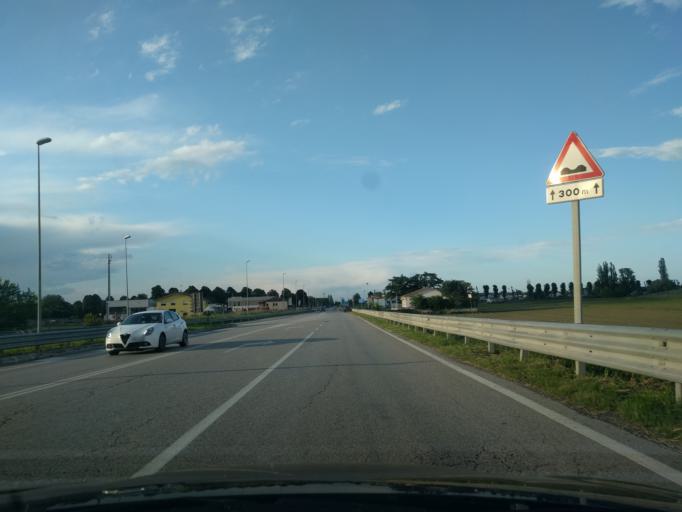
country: IT
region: Veneto
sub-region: Provincia di Rovigo
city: Polesella
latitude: 44.9576
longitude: 11.7392
